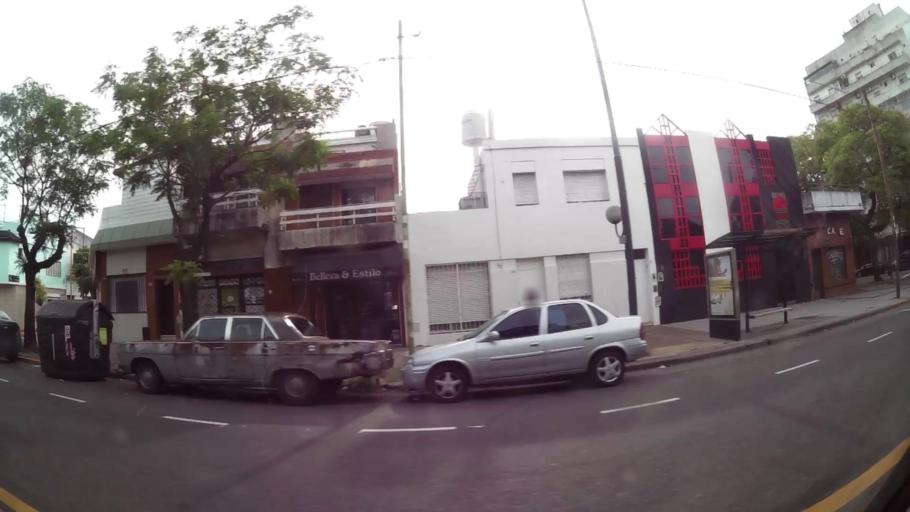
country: AR
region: Buenos Aires F.D.
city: Villa Lugano
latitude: -34.6418
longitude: -58.4312
